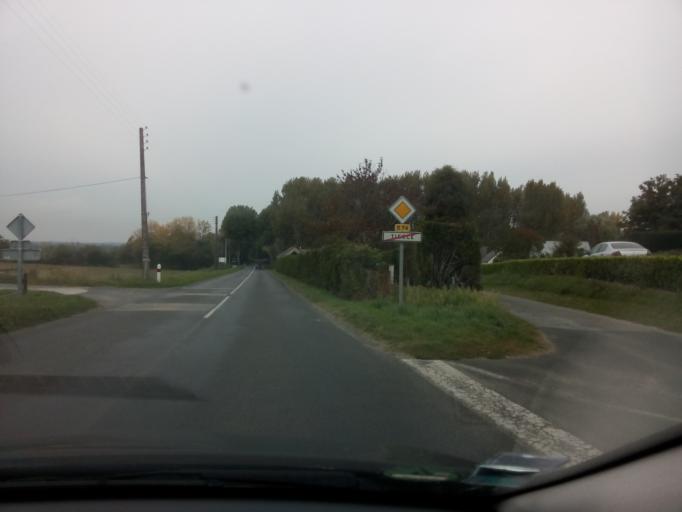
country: FR
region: Pays de la Loire
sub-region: Departement de Maine-et-Loire
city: Tierce
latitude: 47.6152
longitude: -0.4756
